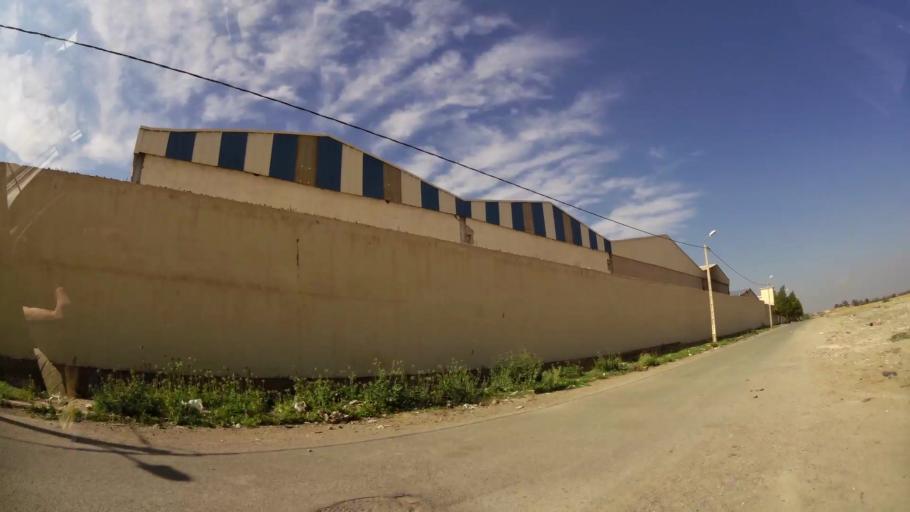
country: MA
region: Oriental
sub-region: Oujda-Angad
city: Oujda
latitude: 34.7003
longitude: -1.8823
